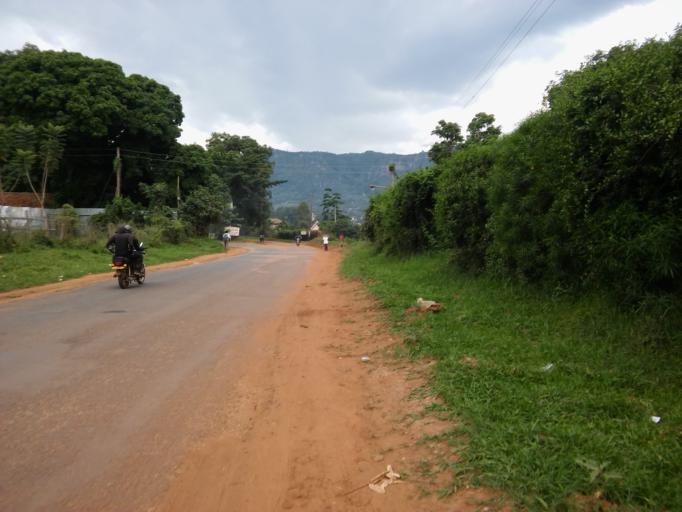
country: UG
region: Eastern Region
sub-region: Mbale District
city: Mbale
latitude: 1.0666
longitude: 34.1908
